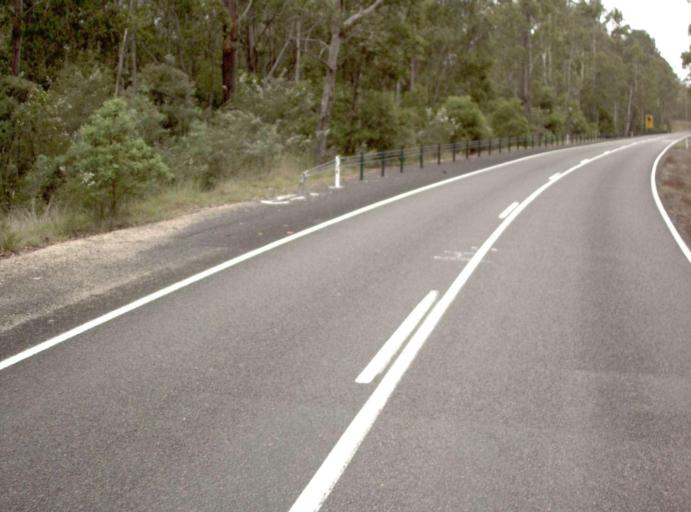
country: AU
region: New South Wales
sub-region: Bombala
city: Bombala
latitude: -37.2865
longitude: 149.2224
